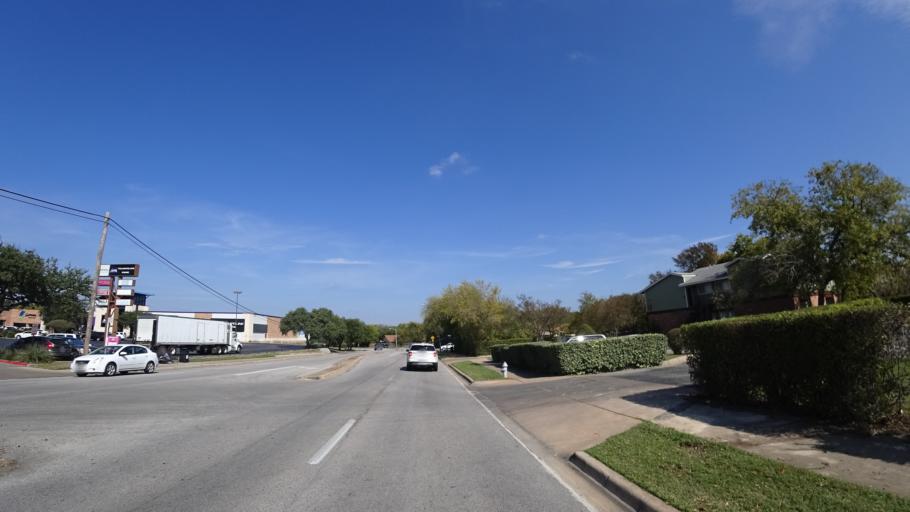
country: US
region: Texas
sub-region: Travis County
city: Shady Hollow
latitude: 30.2080
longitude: -97.8148
